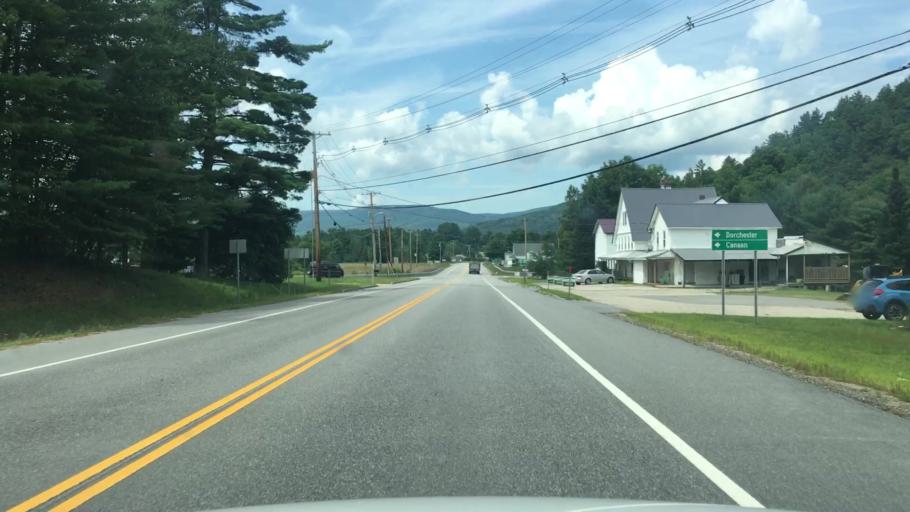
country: US
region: New Hampshire
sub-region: Grafton County
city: Rumney
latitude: 43.8192
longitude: -71.8827
